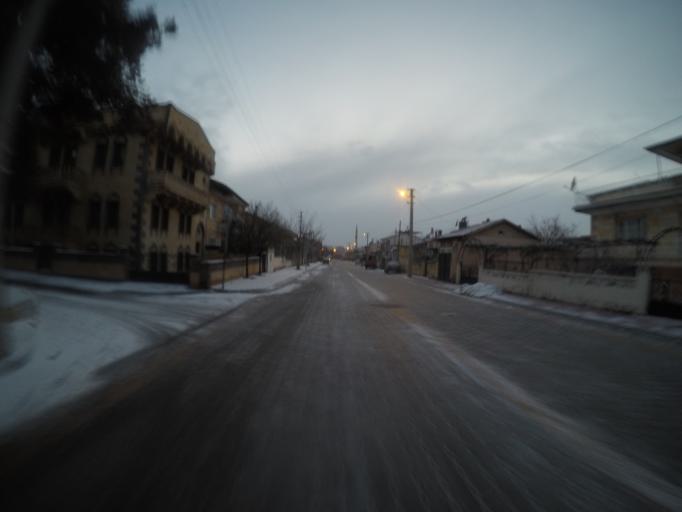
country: TR
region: Nevsehir
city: Goereme
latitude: 38.6268
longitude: 34.8025
